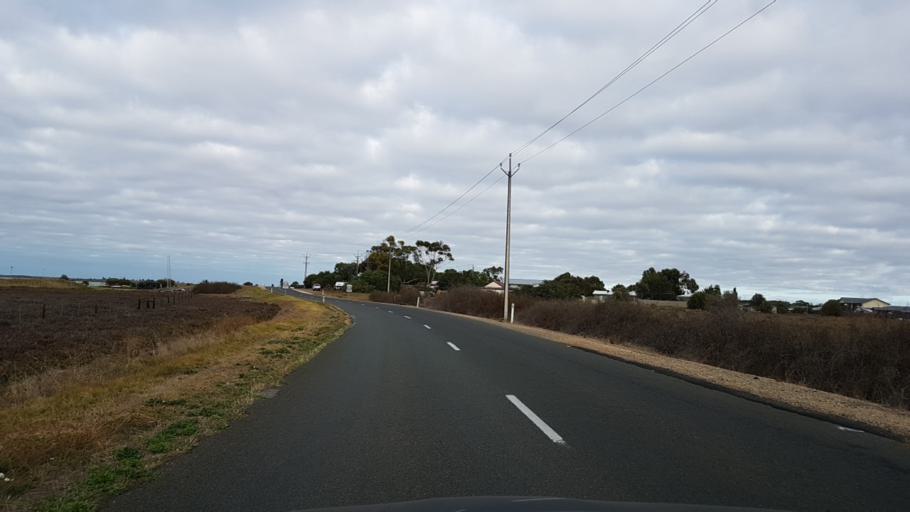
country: AU
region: South Australia
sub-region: Alexandrina
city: Langhorne Creek
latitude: -35.4005
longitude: 138.9836
